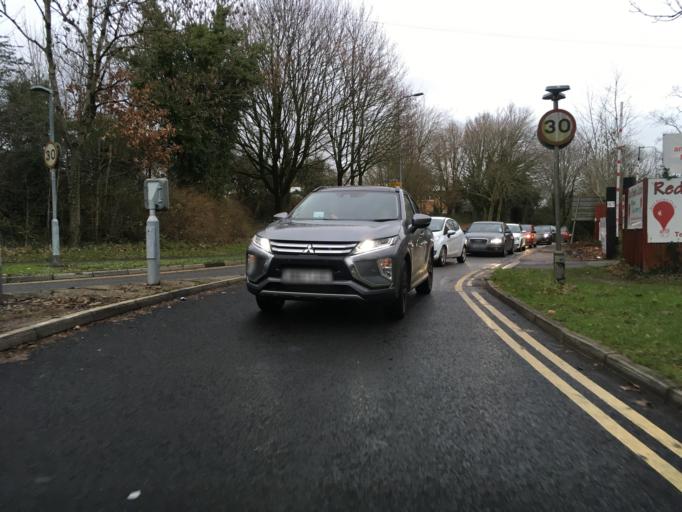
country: GB
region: Wales
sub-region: Cardiff
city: Cardiff
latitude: 51.5078
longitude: -3.1484
